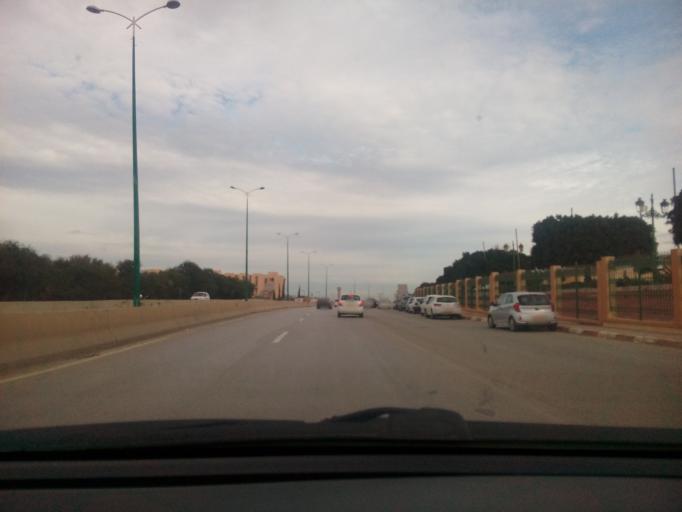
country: DZ
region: Tlemcen
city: Mansoura
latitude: 34.8953
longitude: -1.3556
